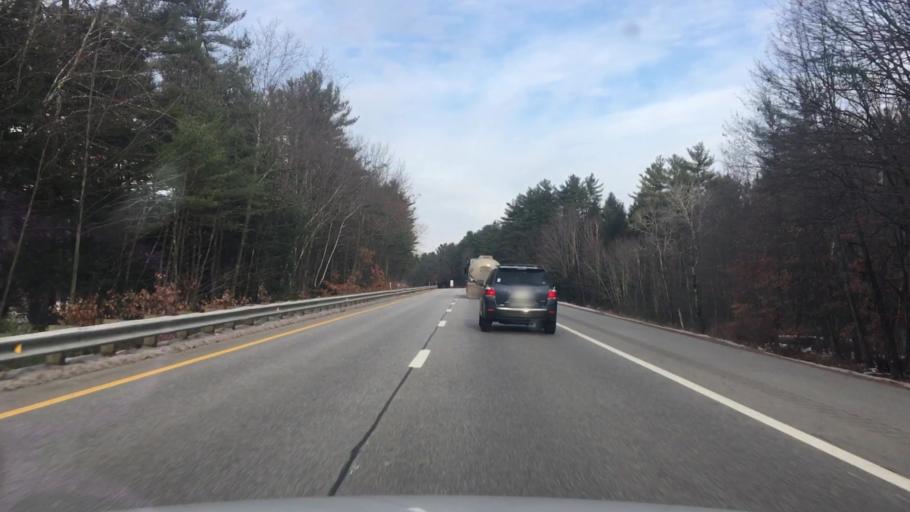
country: US
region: New Hampshire
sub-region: Merrimack County
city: Contoocook
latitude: 43.2091
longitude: -71.7124
